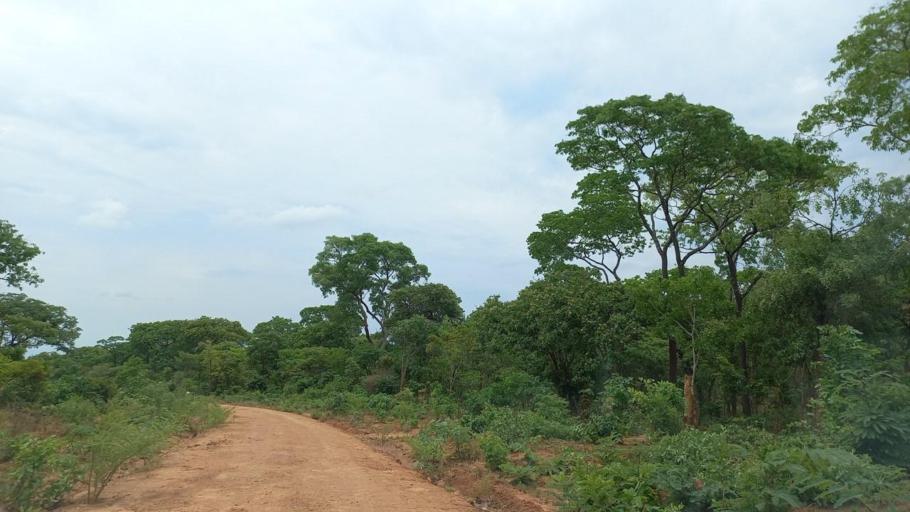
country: ZM
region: North-Western
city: Kalengwa
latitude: -13.6325
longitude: 24.9787
